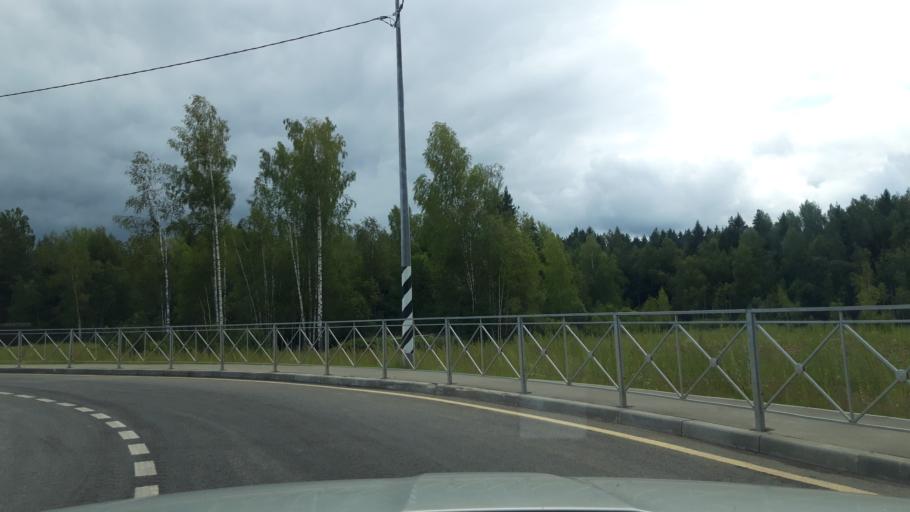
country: RU
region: Moskovskaya
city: Lozhki
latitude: 56.0801
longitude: 37.0910
